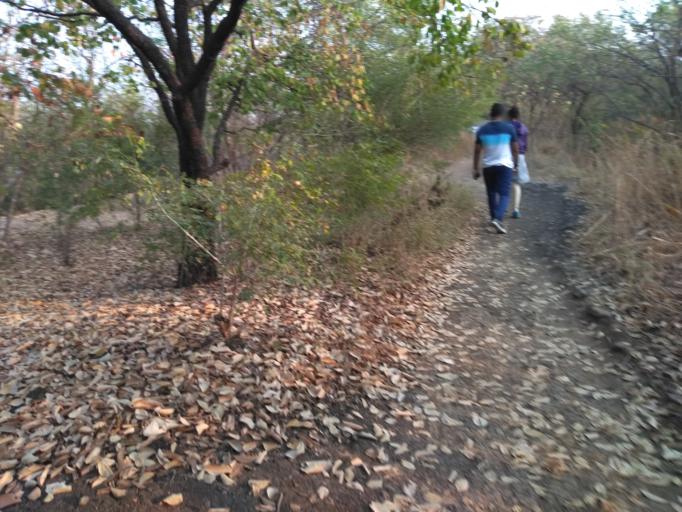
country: IN
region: Maharashtra
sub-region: Pune Division
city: Pune
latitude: 18.4723
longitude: 73.8405
